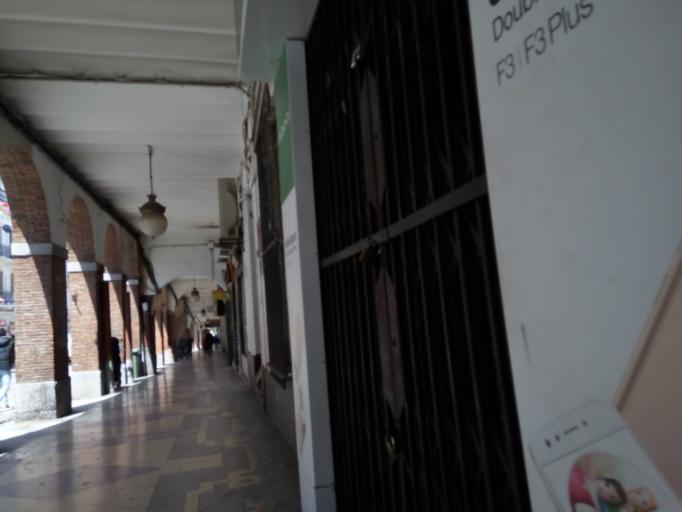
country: DZ
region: Constantine
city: Constantine
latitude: 36.3624
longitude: 6.6078
